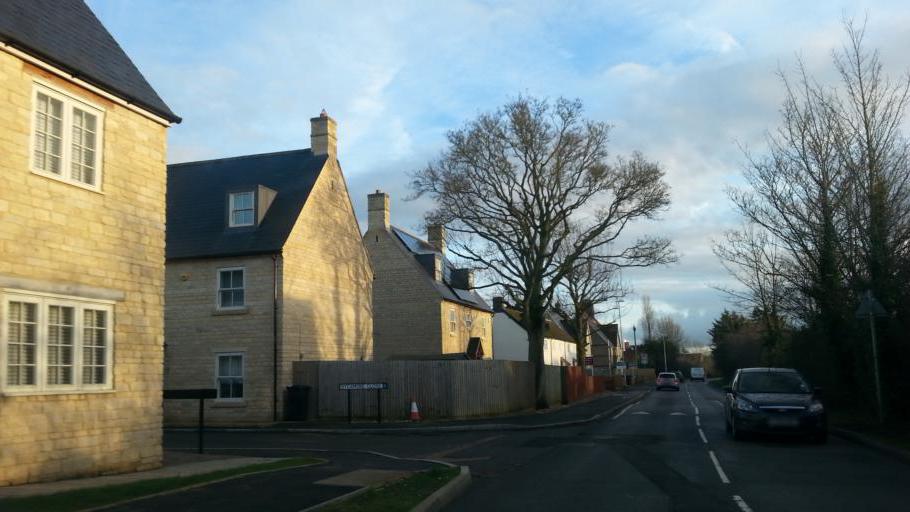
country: GB
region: England
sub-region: Northamptonshire
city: Brackley
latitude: 52.0429
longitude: -1.1528
